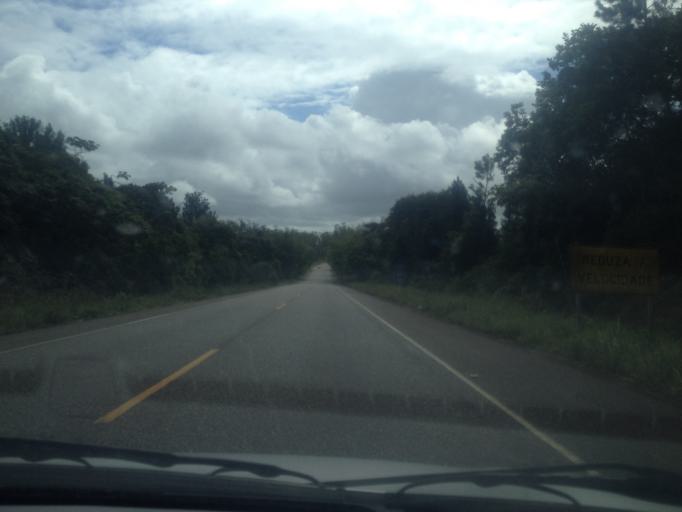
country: BR
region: Bahia
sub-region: Entre Rios
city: Entre Rios
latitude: -12.3131
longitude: -37.9044
